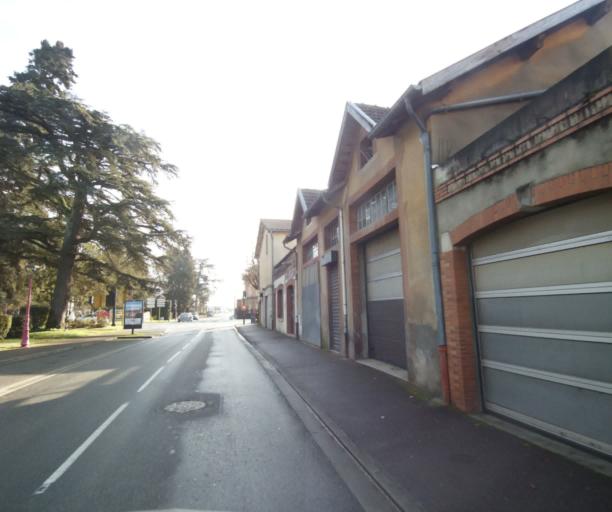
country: FR
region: Midi-Pyrenees
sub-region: Departement de la Haute-Garonne
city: Villemur-sur-Tarn
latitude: 43.8617
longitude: 1.5029
